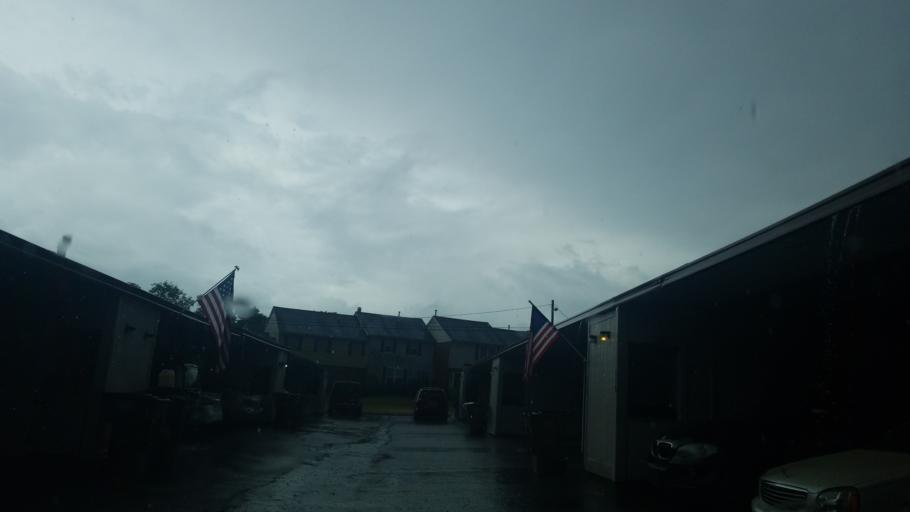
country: US
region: Tennessee
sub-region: Rutherford County
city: La Vergne
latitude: 36.1060
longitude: -86.5996
